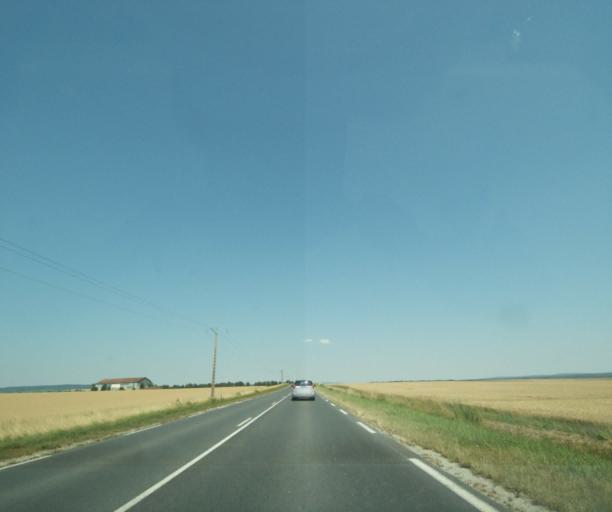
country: FR
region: Champagne-Ardenne
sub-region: Departement de la Marne
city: Mourmelon-le-Grand
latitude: 49.0811
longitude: 4.2822
